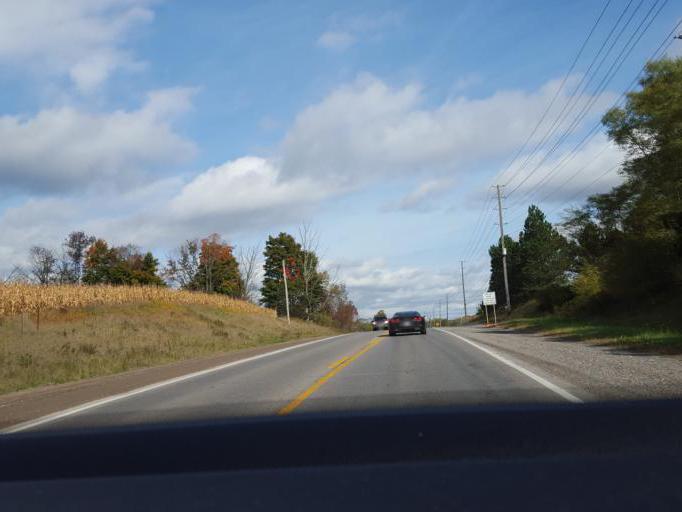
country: CA
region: Ontario
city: Oshawa
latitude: 43.9578
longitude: -78.7703
